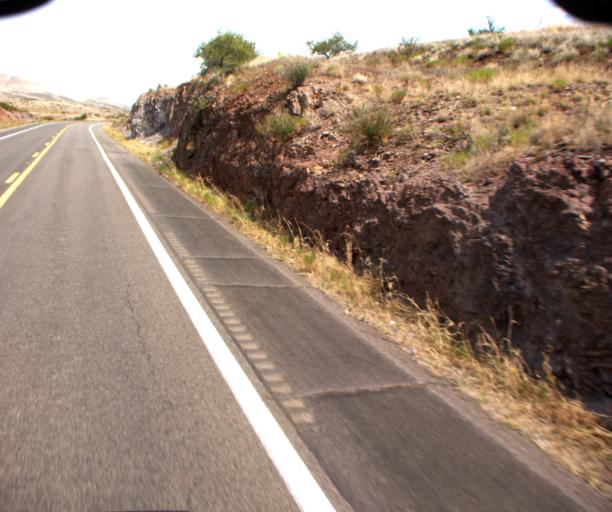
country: US
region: Arizona
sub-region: Greenlee County
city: Clifton
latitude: 32.7498
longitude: -109.2327
